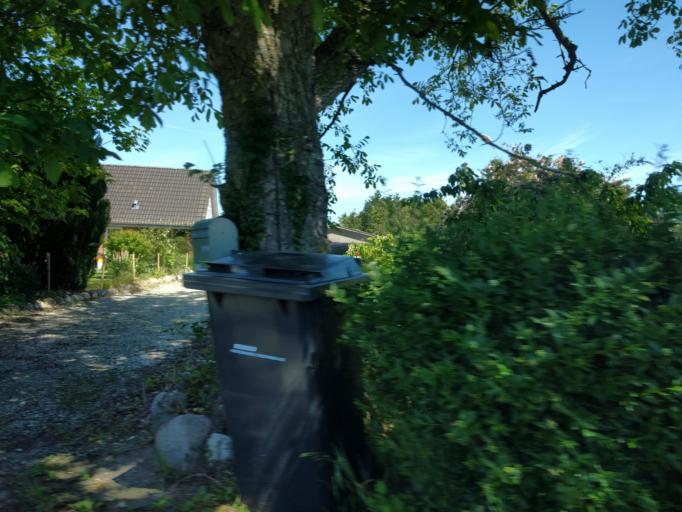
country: DK
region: South Denmark
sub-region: Kerteminde Kommune
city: Langeskov
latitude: 55.3417
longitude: 10.5936
